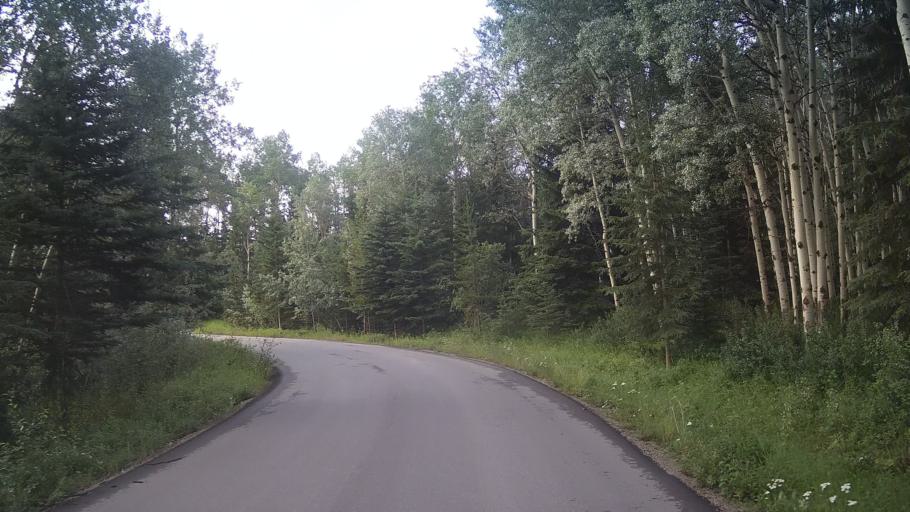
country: CA
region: Alberta
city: Jasper Park Lodge
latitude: 52.9649
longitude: -118.0601
